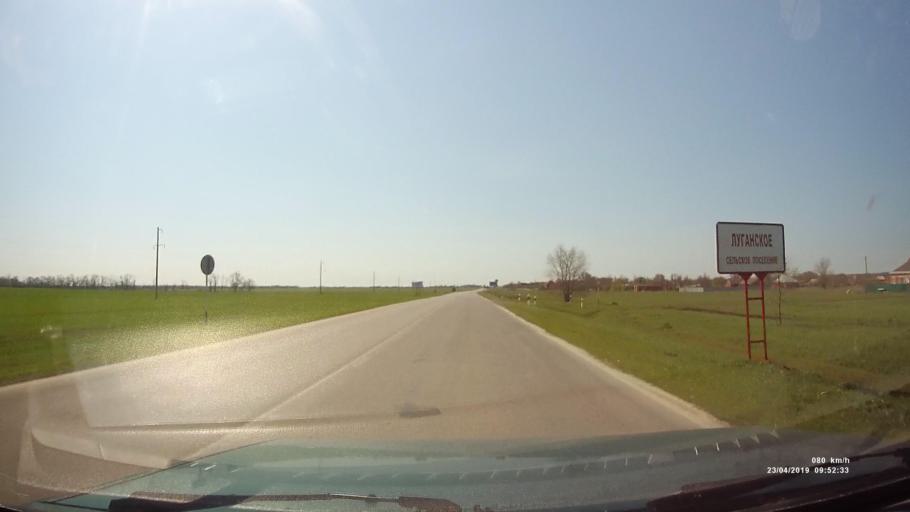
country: RU
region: Rostov
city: Orlovskiy
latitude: 46.8433
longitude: 42.0464
